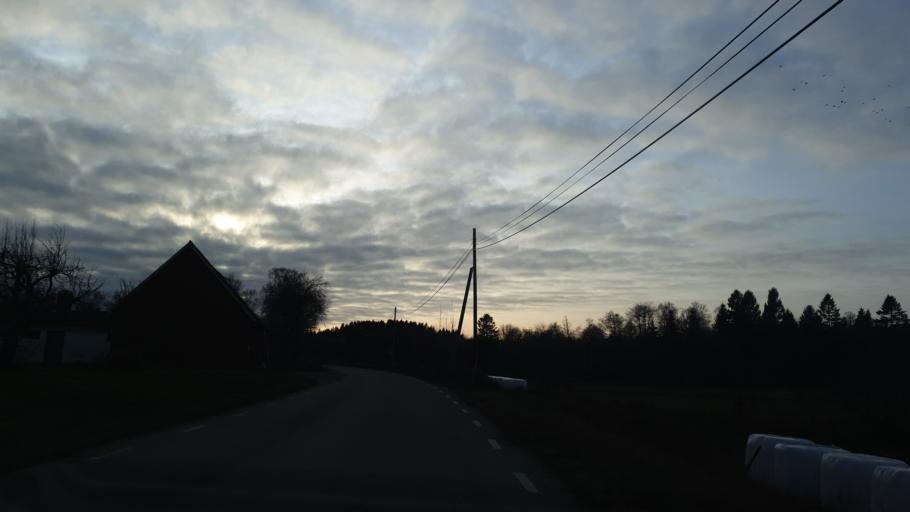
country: SE
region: Blekinge
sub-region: Karlskrona Kommun
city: Jaemjoe
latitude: 56.1835
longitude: 15.9401
